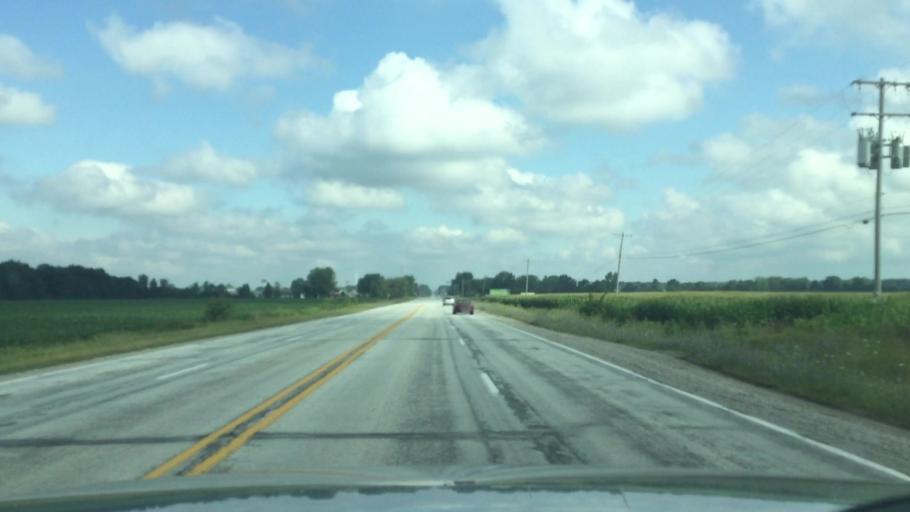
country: US
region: Michigan
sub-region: Saginaw County
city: Birch Run
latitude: 43.2377
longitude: -83.7599
